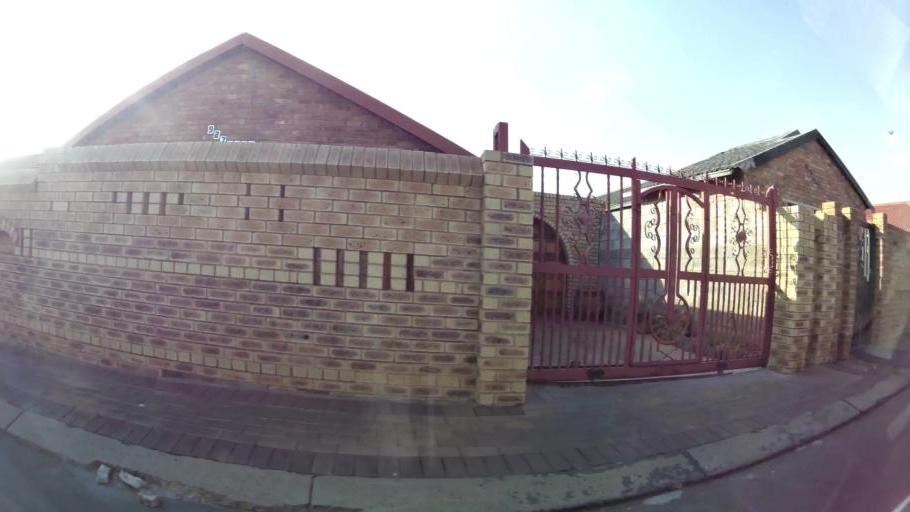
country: ZA
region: Gauteng
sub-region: City of Johannesburg Metropolitan Municipality
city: Soweto
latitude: -26.2668
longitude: 27.9157
